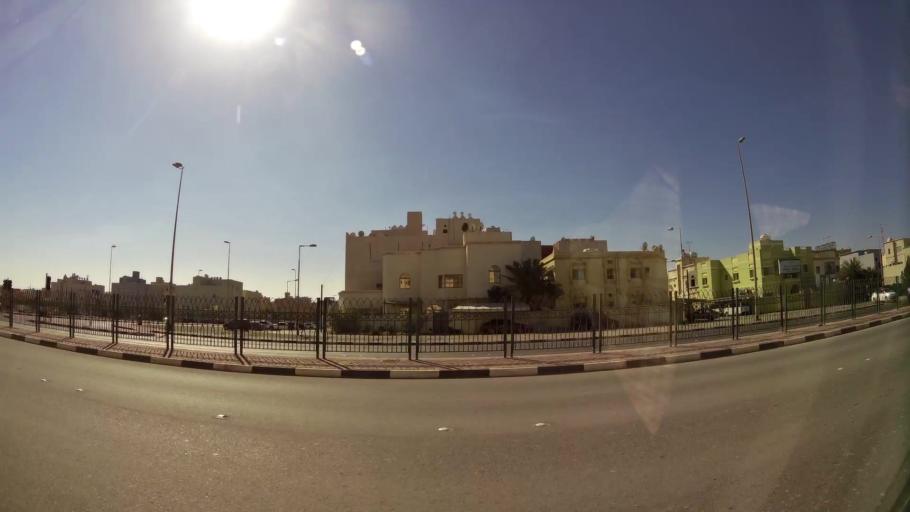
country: BH
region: Muharraq
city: Al Hadd
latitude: 26.2345
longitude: 50.6523
